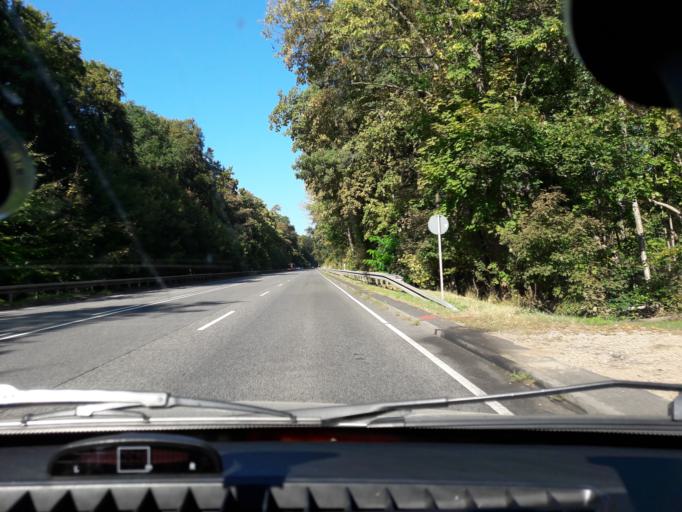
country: DE
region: Hesse
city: Taunusstein
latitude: 50.1086
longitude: 8.1926
